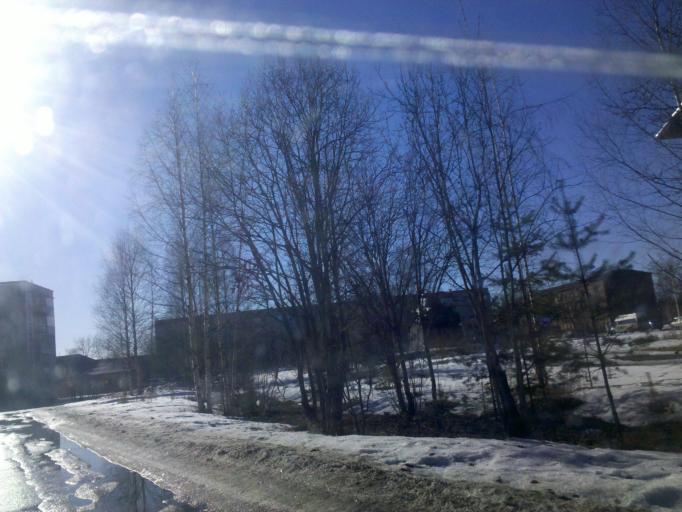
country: RU
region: Republic of Karelia
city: Medvezh'yegorsk
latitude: 62.9153
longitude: 34.4755
